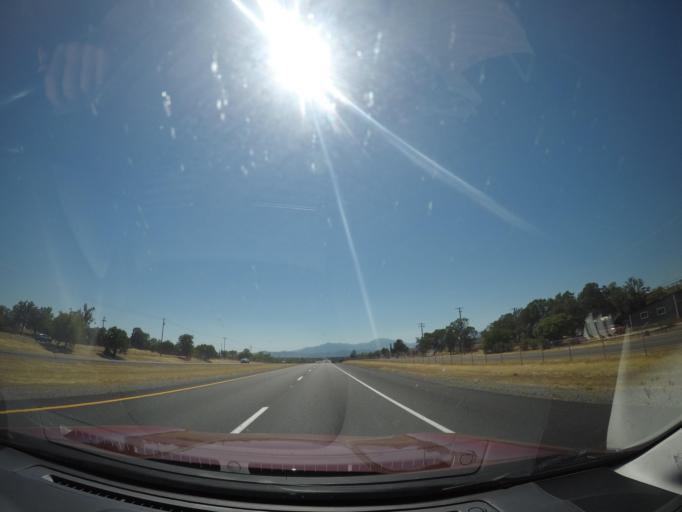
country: US
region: California
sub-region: Shasta County
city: Redding
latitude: 40.6174
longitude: -122.3357
